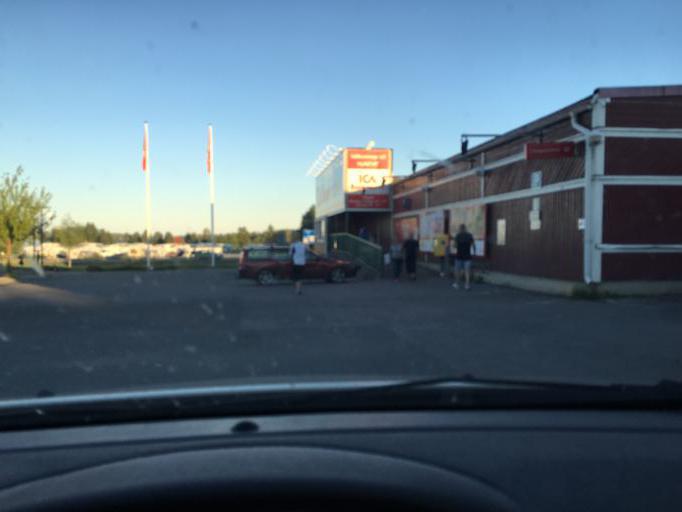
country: SE
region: Norrbotten
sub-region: Kalix Kommun
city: Kalix
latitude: 65.8548
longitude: 23.1379
